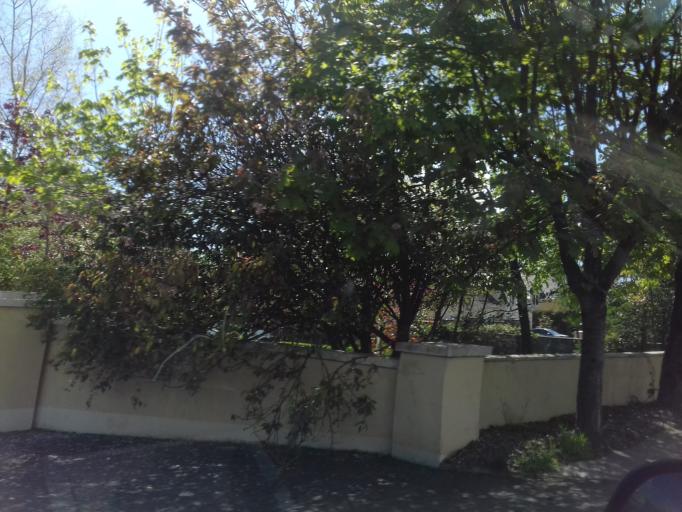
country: IE
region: Leinster
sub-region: Loch Garman
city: Castlebridge
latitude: 52.3793
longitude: -6.4505
